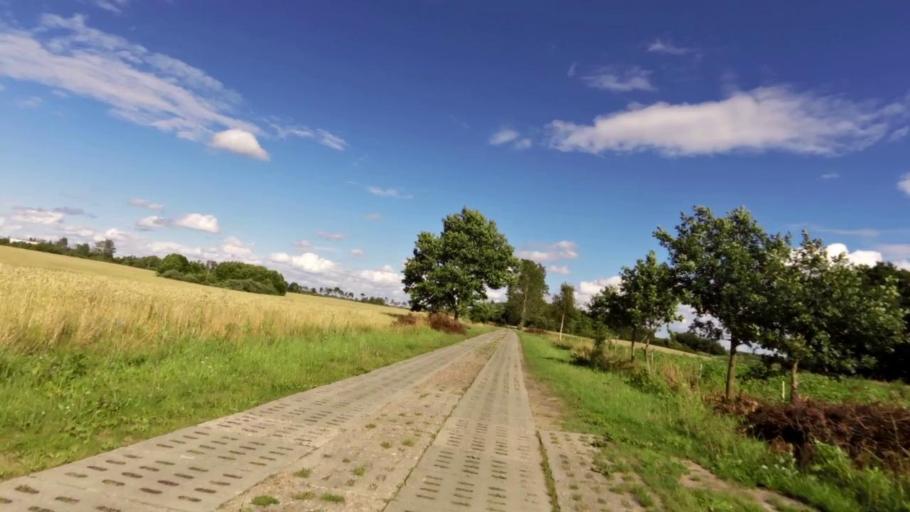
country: PL
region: West Pomeranian Voivodeship
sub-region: Powiat slawienski
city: Slawno
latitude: 54.4627
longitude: 16.7226
